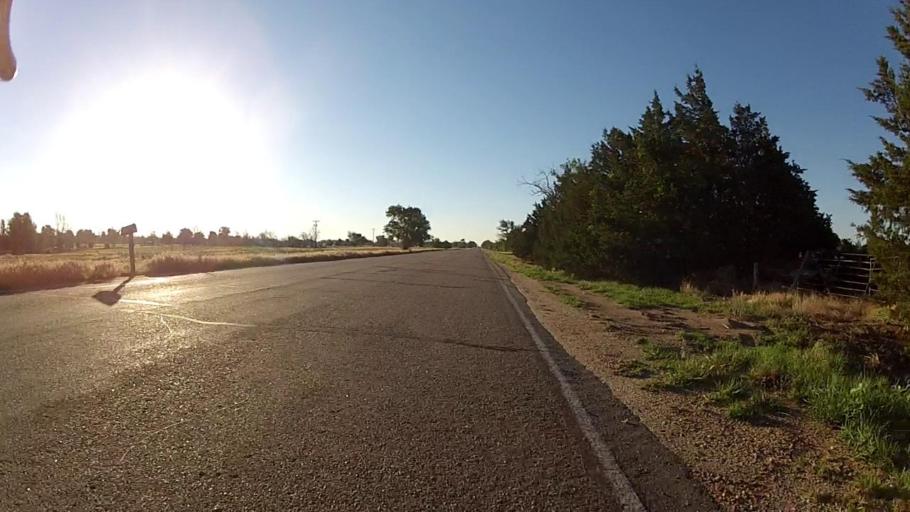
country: US
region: Kansas
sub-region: Ford County
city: Dodge City
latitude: 37.7165
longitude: -99.9372
